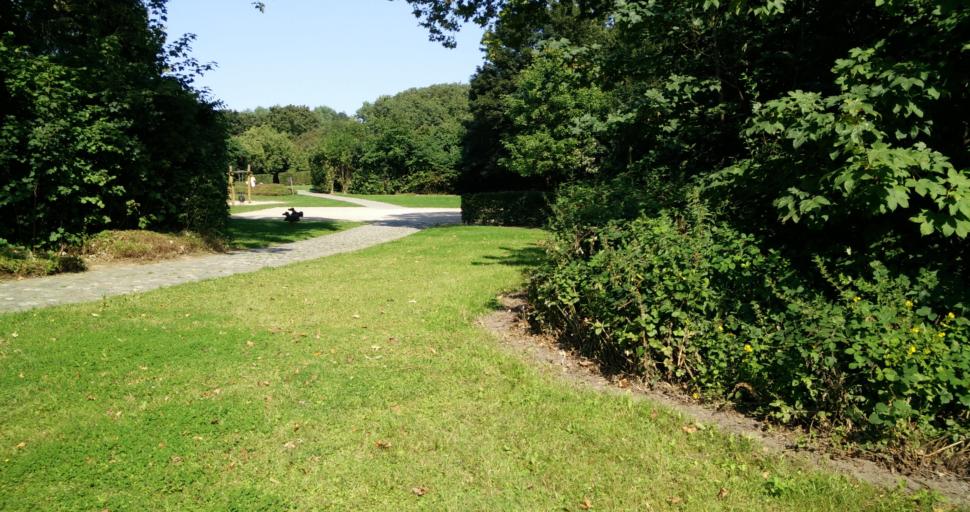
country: BE
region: Flanders
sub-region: Provincie Vlaams-Brabant
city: Halle
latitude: 50.7128
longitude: 4.2246
